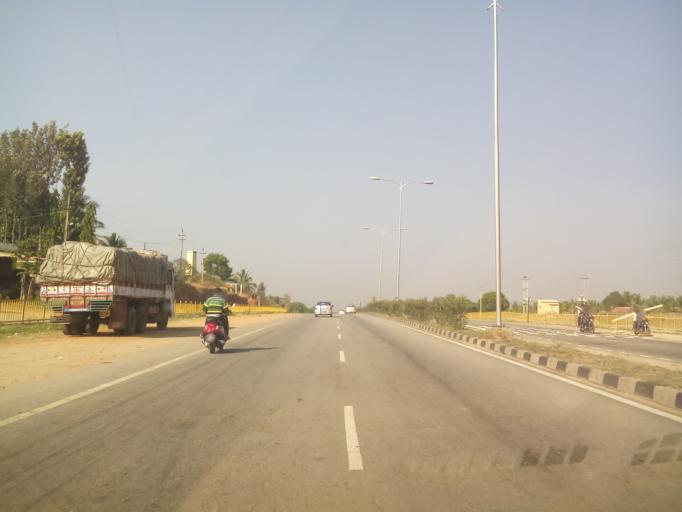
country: IN
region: Karnataka
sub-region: Ramanagara
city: Magadi
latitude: 13.0573
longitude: 77.1593
